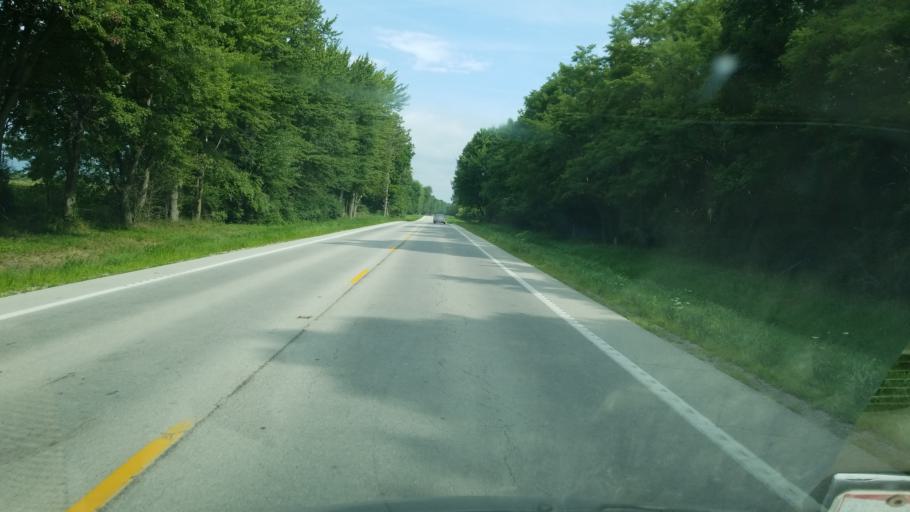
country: US
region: Ohio
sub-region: Sandusky County
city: Ballville
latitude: 41.2648
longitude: -83.1681
